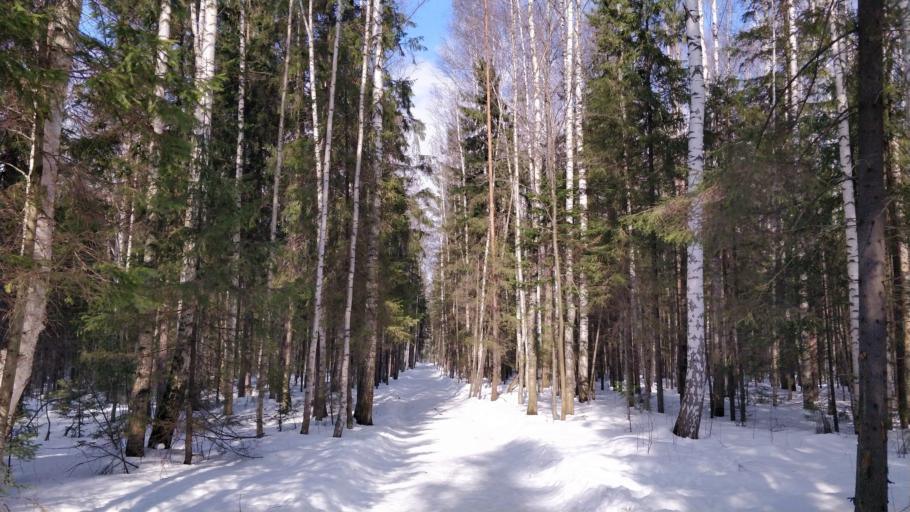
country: RU
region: Perm
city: Kondratovo
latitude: 57.9850
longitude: 56.1557
